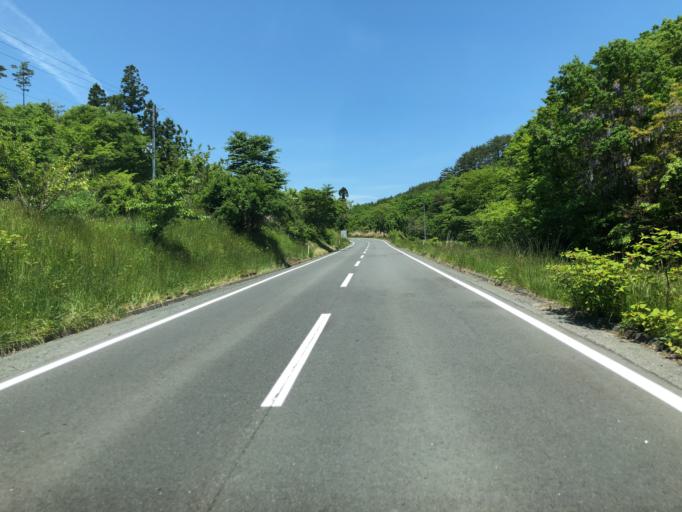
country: JP
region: Fukushima
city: Funehikimachi-funehiki
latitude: 37.5093
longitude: 140.7754
